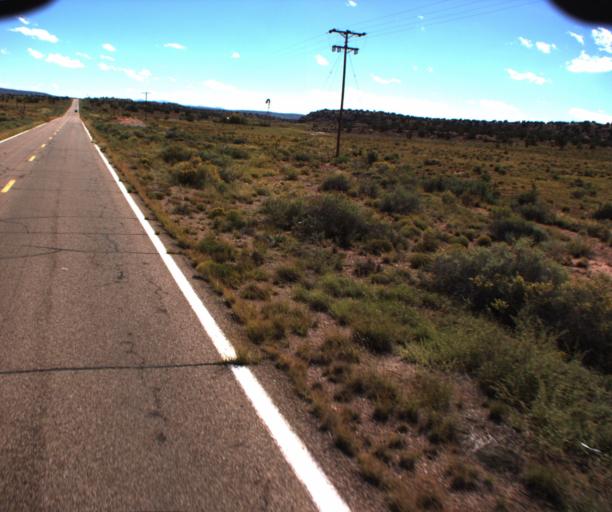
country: US
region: Arizona
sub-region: Apache County
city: Saint Johns
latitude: 34.5505
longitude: -109.6243
